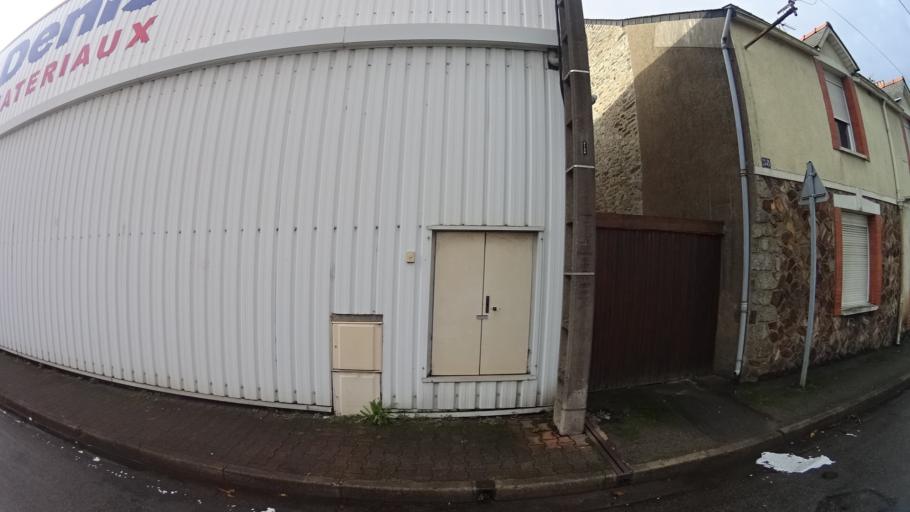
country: FR
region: Brittany
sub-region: Departement d'Ille-et-Vilaine
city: Redon
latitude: 47.6451
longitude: -2.0907
